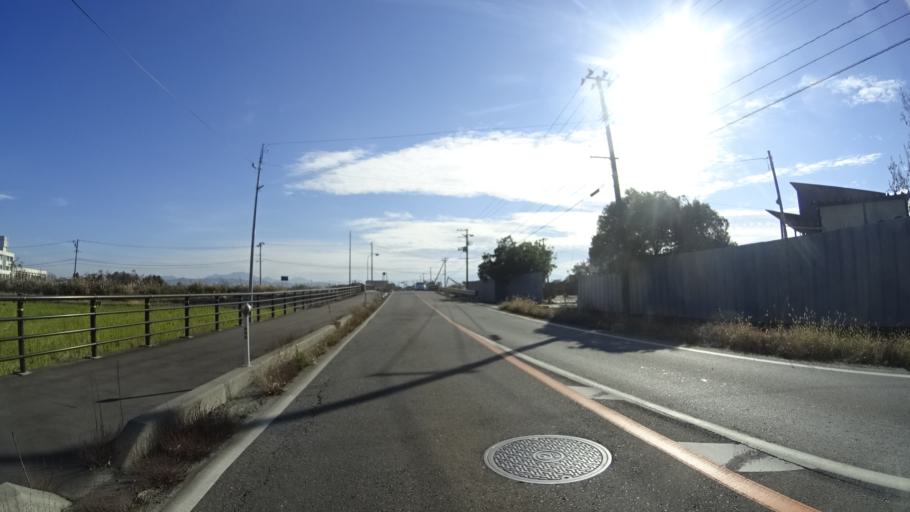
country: JP
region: Niigata
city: Mitsuke
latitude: 37.5533
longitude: 138.8611
